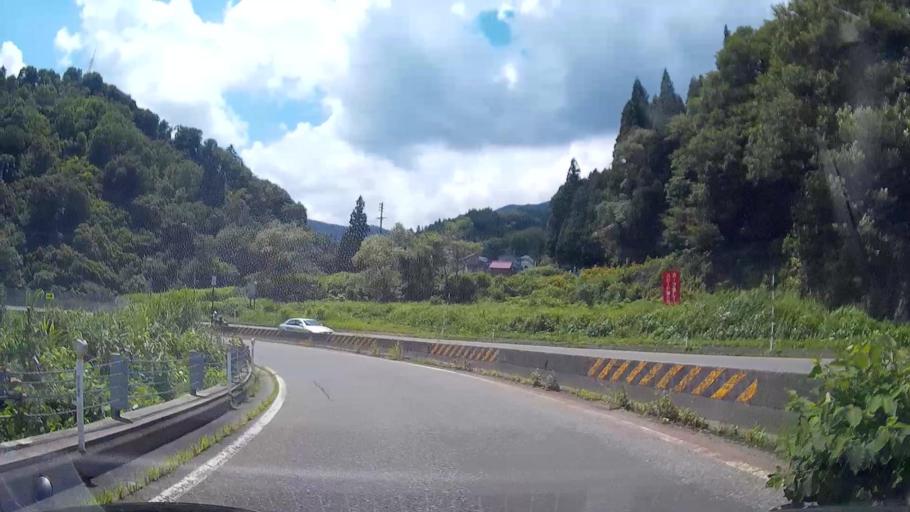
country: JP
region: Niigata
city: Shiozawa
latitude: 36.9215
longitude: 138.8126
